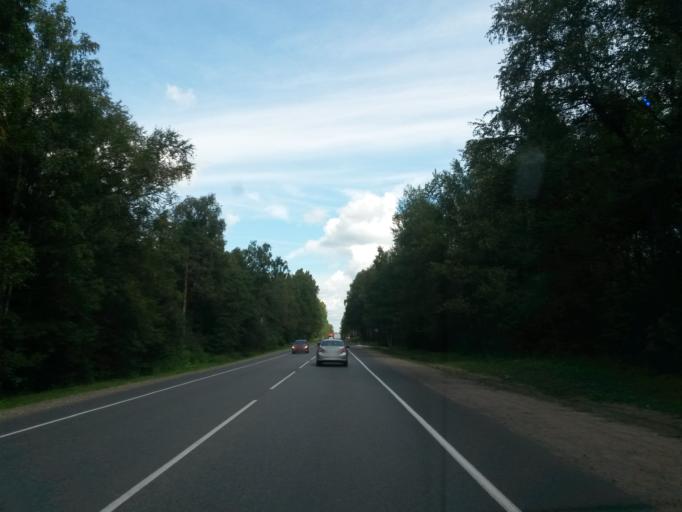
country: RU
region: Jaroslavl
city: Pereslavl'-Zalesskiy
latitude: 56.8140
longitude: 38.9015
